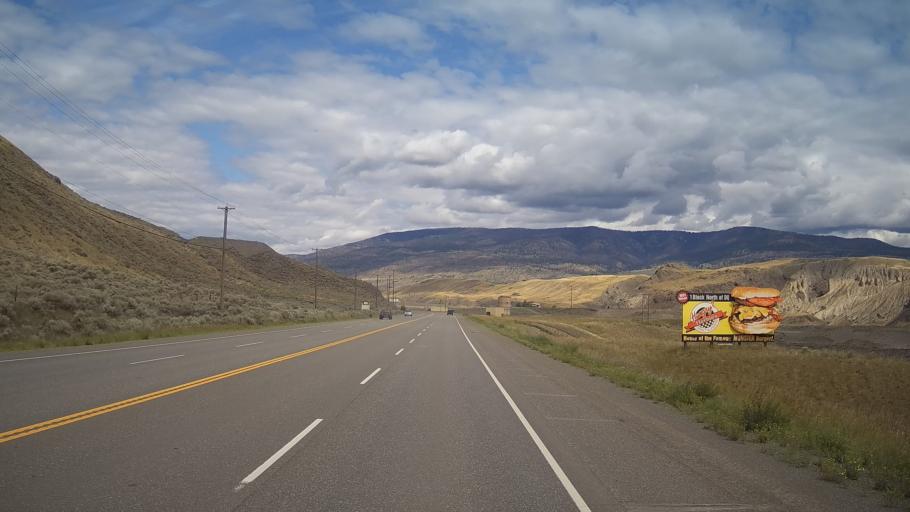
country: CA
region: British Columbia
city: Cache Creek
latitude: 50.7793
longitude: -121.3125
